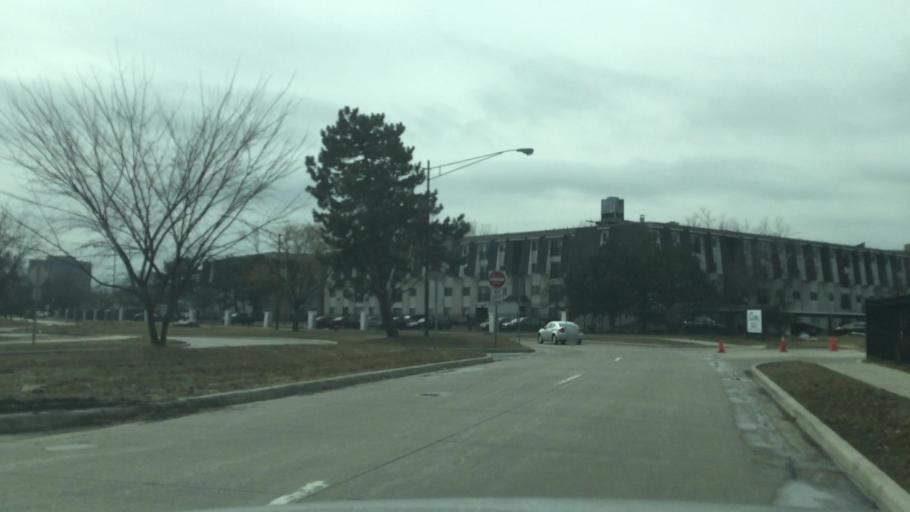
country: US
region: Michigan
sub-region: Oakland County
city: Southfield
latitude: 42.4612
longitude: -83.2065
